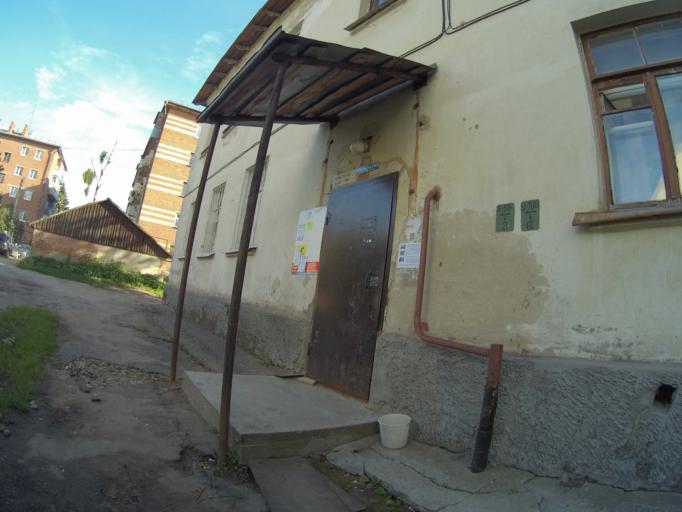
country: RU
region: Vladimir
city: Vladimir
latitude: 56.1487
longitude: 40.4301
